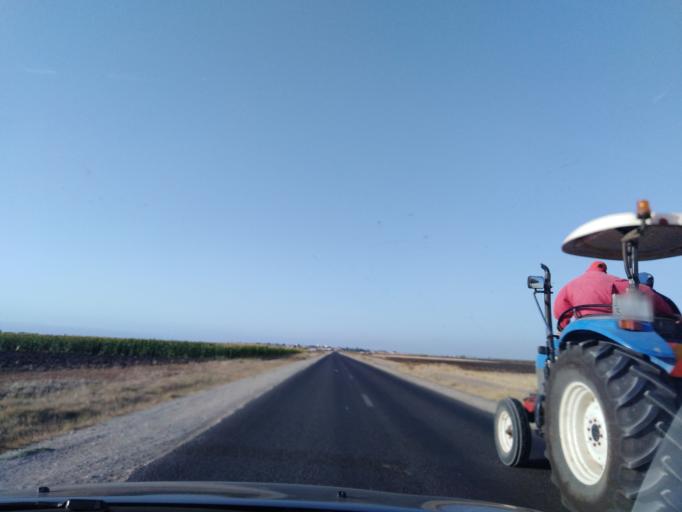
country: MA
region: Doukkala-Abda
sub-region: Safi
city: Safi
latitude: 32.5129
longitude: -8.9158
